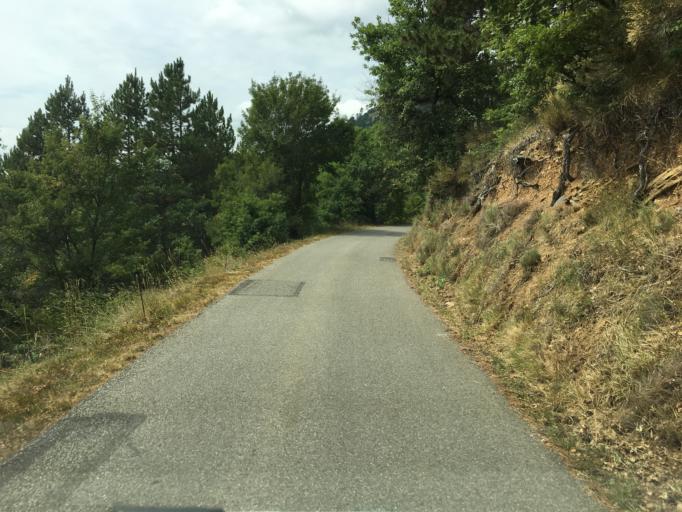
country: FR
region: Provence-Alpes-Cote d'Azur
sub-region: Departement des Alpes-de-Haute-Provence
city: Digne-les-Bains
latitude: 44.1982
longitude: 6.1435
